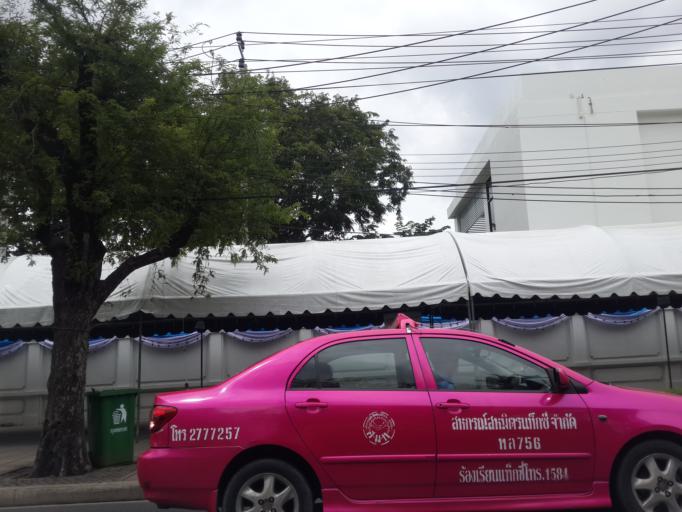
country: TH
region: Bangkok
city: Pom Prap Sattru Phai
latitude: 13.7678
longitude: 100.5125
